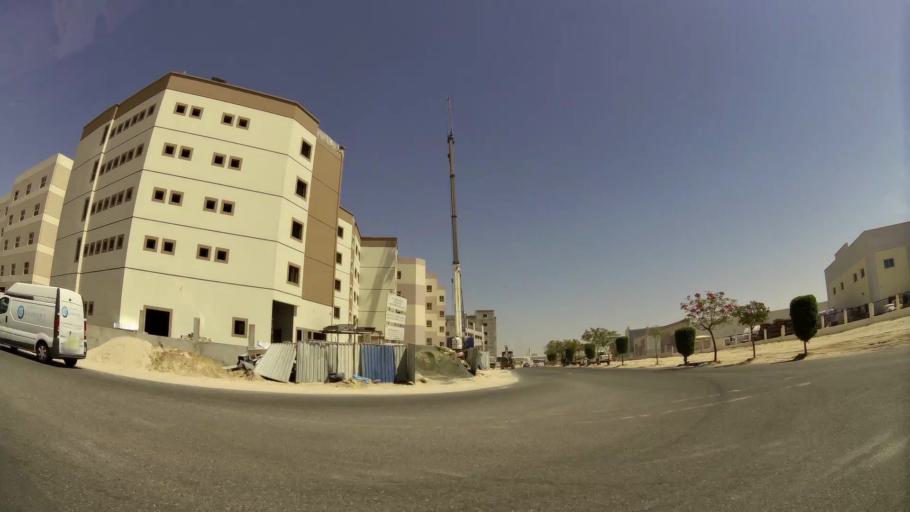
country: AE
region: Dubai
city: Dubai
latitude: 24.9748
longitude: 55.2070
